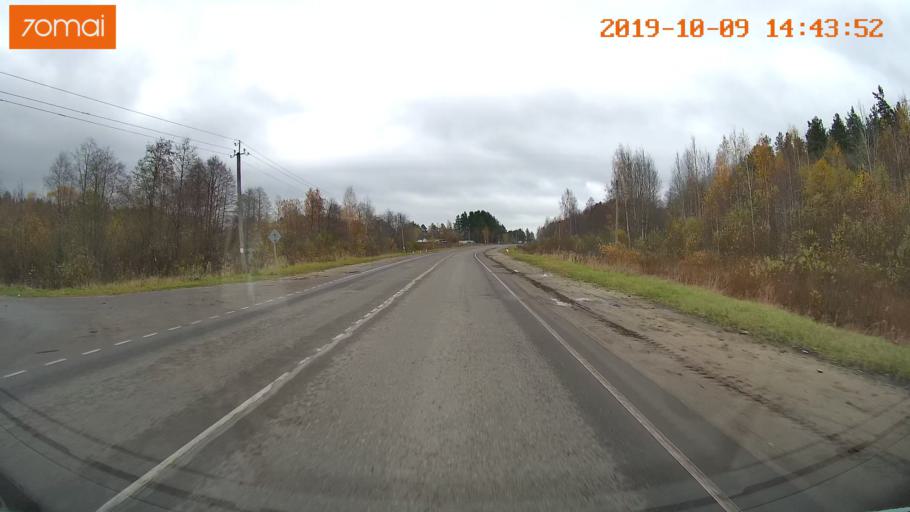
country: RU
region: Kostroma
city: Buy
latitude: 58.4558
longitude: 41.5530
